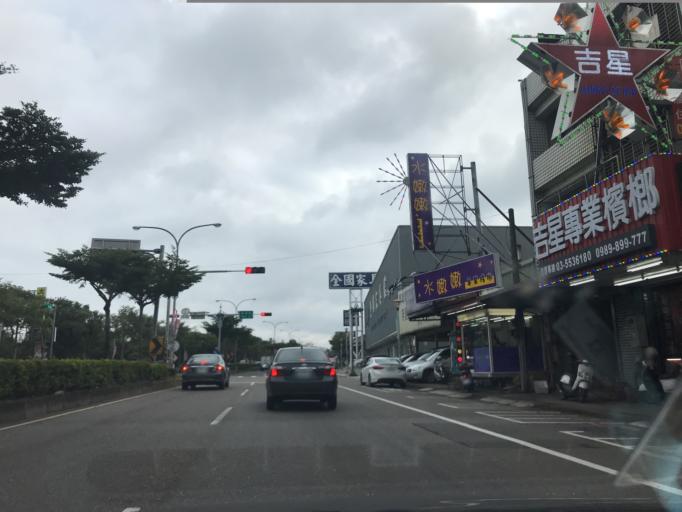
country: TW
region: Taiwan
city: Daxi
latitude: 24.9391
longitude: 121.2163
